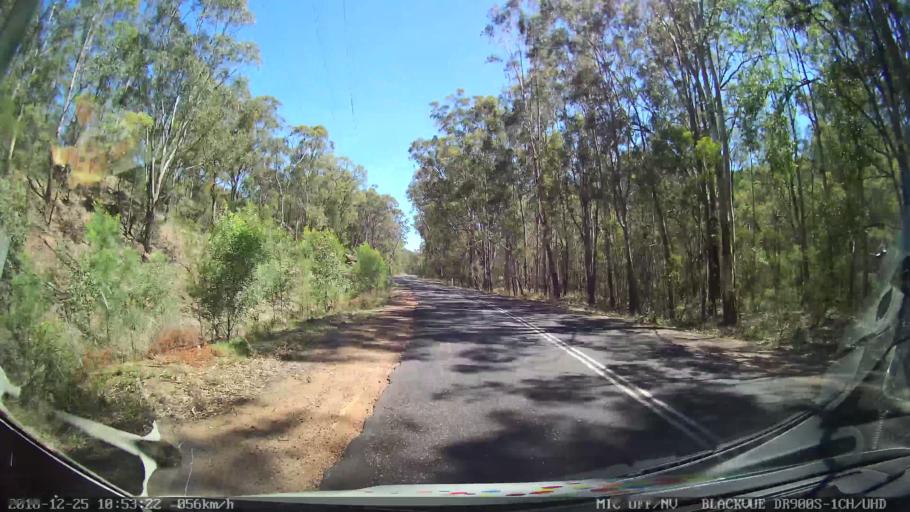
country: AU
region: New South Wales
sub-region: Upper Hunter Shire
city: Merriwa
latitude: -32.4208
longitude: 150.2734
